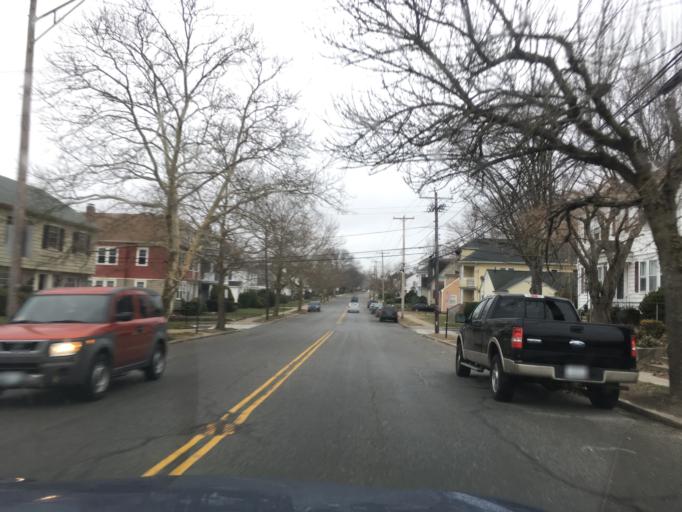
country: US
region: Rhode Island
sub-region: Providence County
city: North Providence
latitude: 41.8372
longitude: -71.4511
